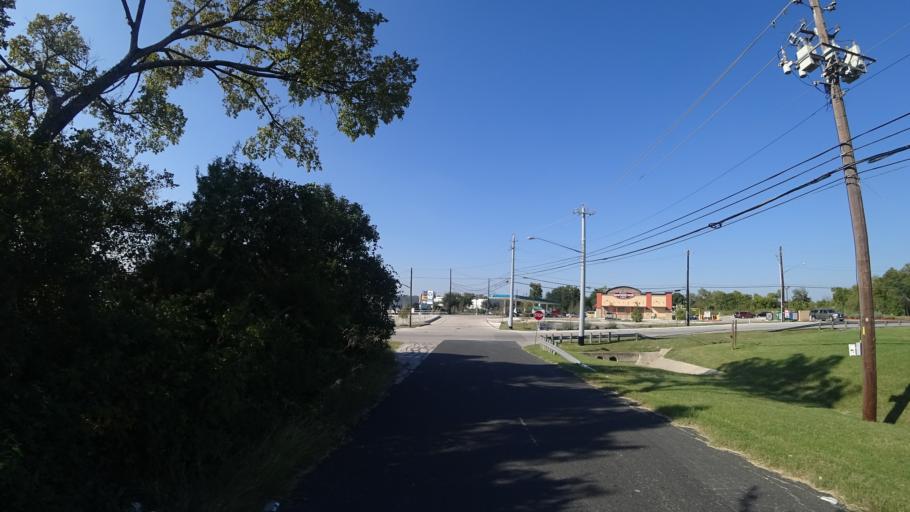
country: US
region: Texas
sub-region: Travis County
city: Wells Branch
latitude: 30.3454
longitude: -97.6767
